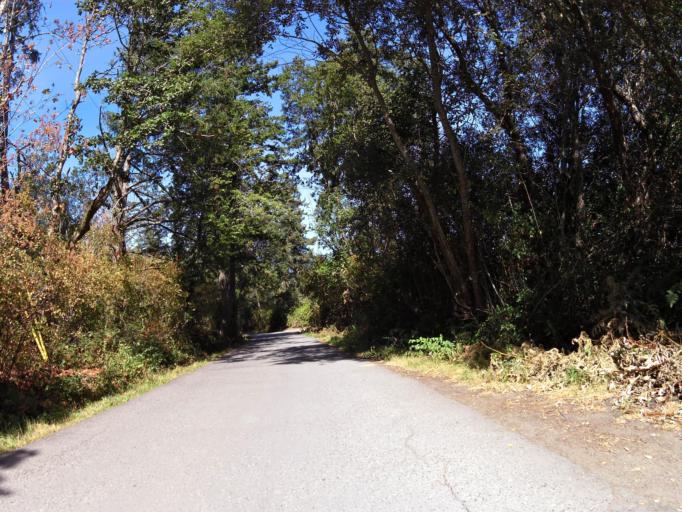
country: CA
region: British Columbia
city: Victoria
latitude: 48.4996
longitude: -123.3604
